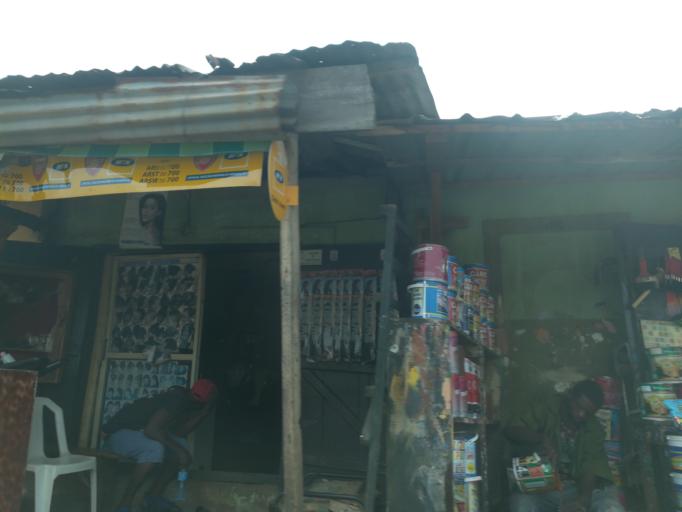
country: NG
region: Lagos
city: Ikorodu
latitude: 6.6106
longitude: 3.5054
